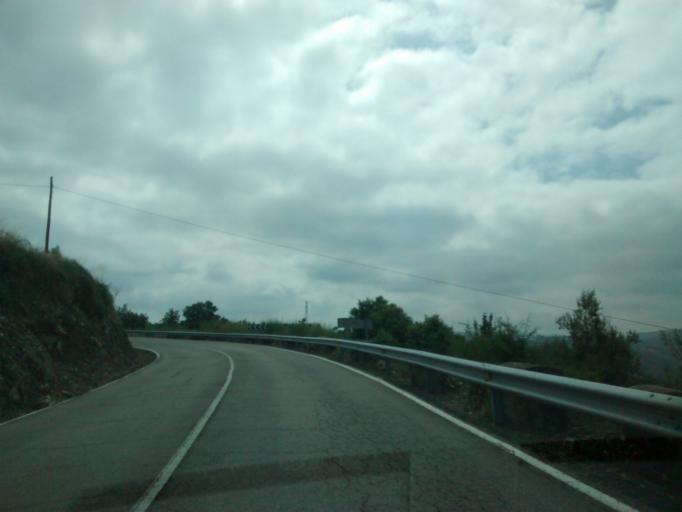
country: ES
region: Galicia
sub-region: Provincia de Ourense
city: Petin
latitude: 42.3441
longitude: -7.1741
